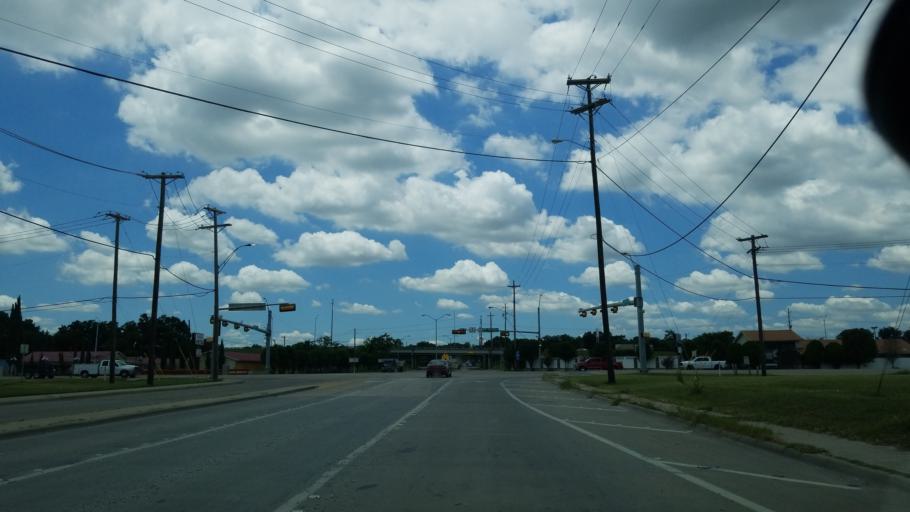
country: US
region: Texas
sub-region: Dallas County
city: Hutchins
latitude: 32.7161
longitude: -96.7547
